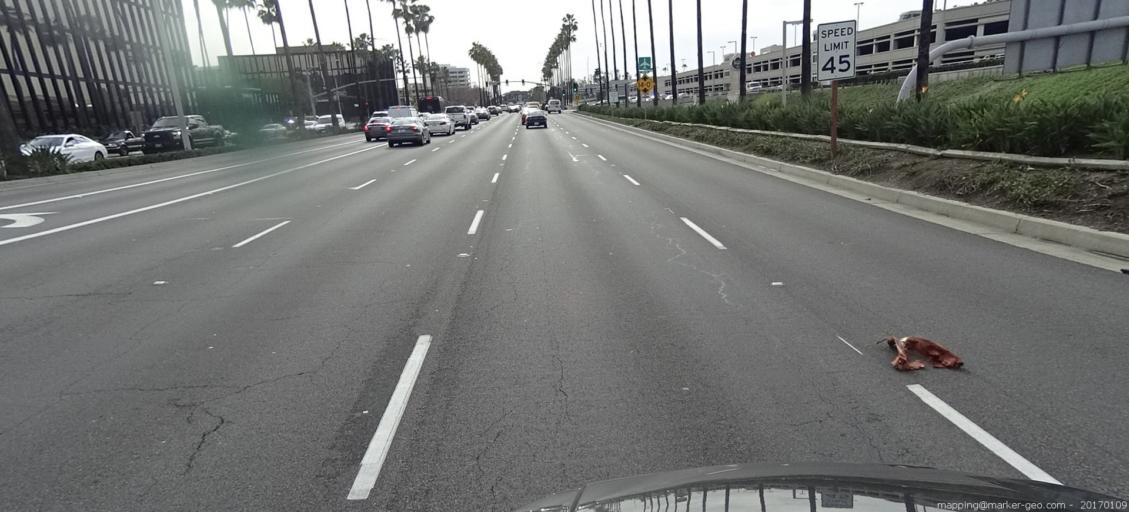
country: US
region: California
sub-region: Orange County
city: Irvine
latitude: 33.6788
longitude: -117.8600
